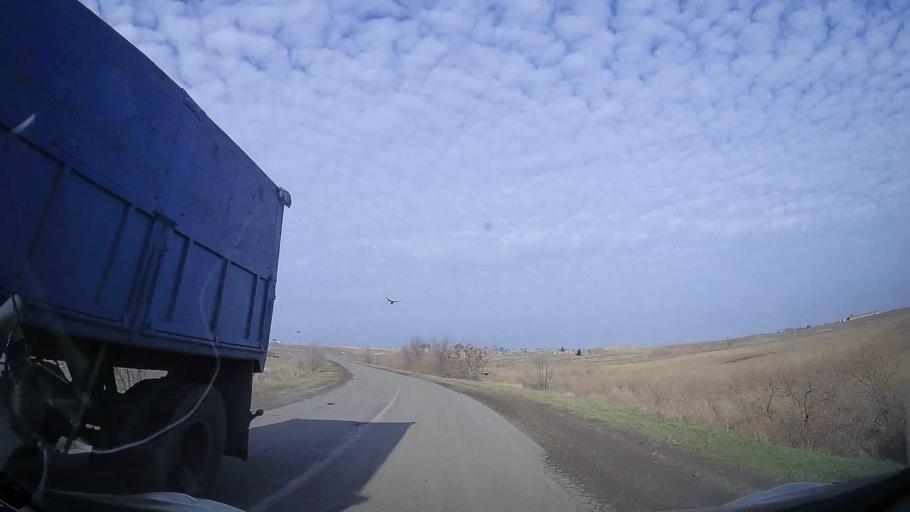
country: RU
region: Rostov
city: Gigant
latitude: 46.8424
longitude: 41.3310
